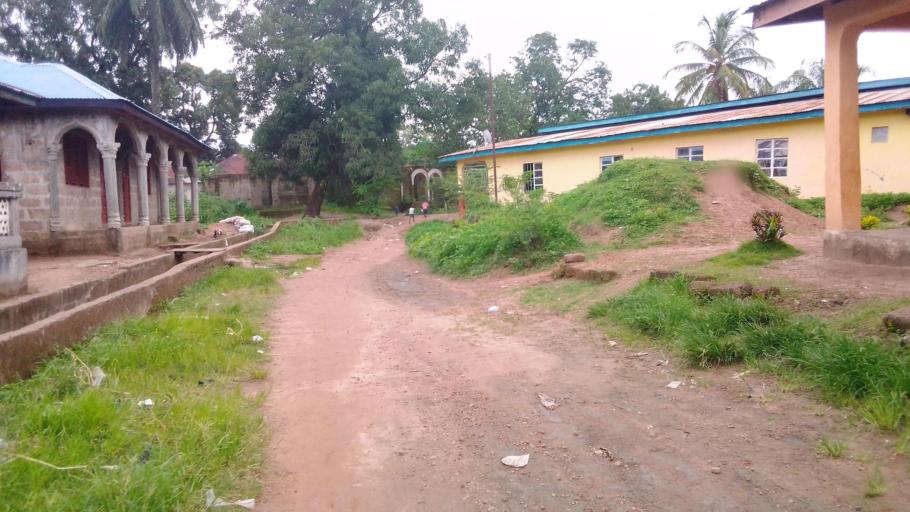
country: SL
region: Northern Province
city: Makeni
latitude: 8.8809
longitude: -12.0412
